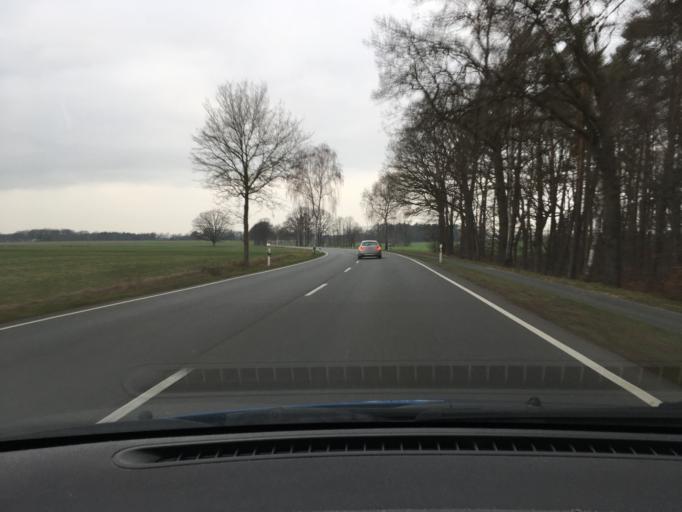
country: DE
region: Lower Saxony
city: Bomlitz
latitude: 52.8619
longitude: 9.6553
